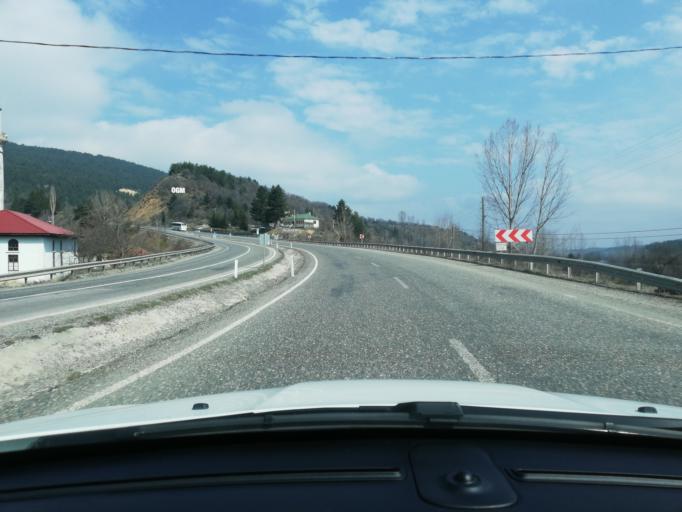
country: TR
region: Kastamonu
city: Kuzyaka
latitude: 41.2019
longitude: 33.7966
